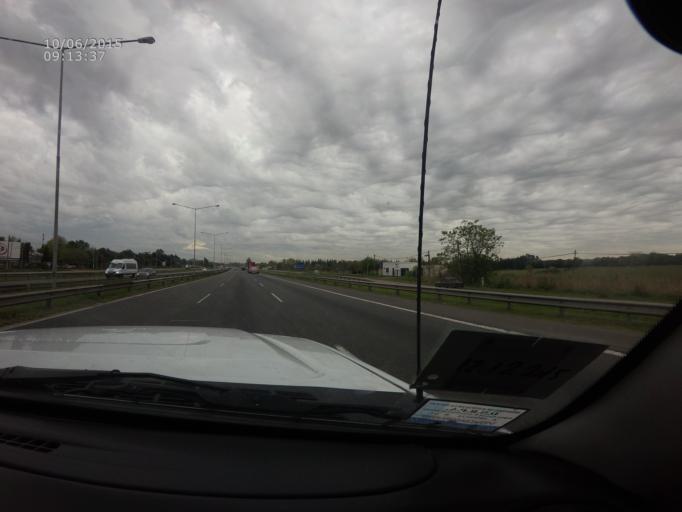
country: AR
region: Buenos Aires
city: Belen de Escobar
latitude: -34.3362
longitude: -58.8220
